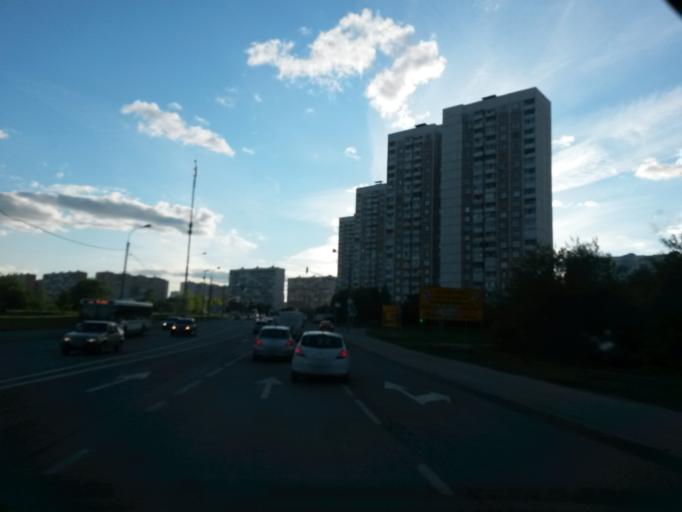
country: RU
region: Moscow
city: Solntsevo
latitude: 55.6400
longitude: 37.3744
